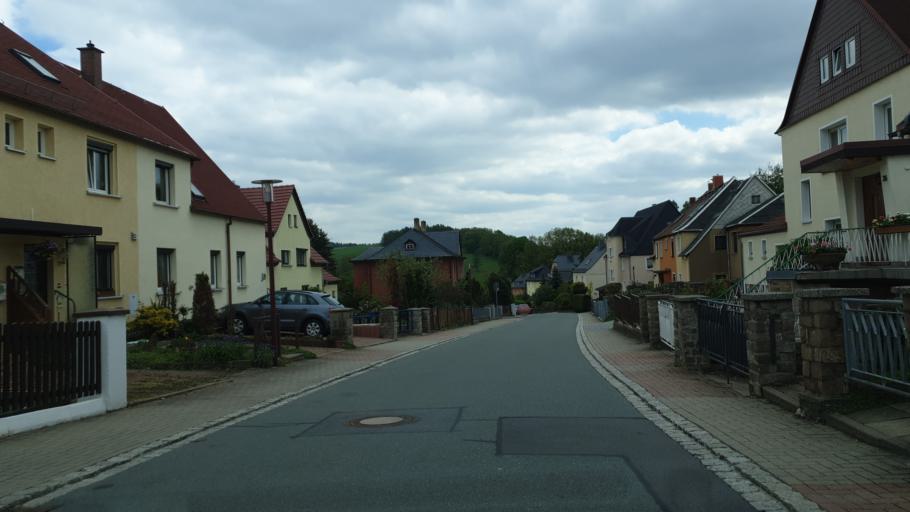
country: DE
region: Saxony
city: Bernsdorf
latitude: 50.7480
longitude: 12.6586
